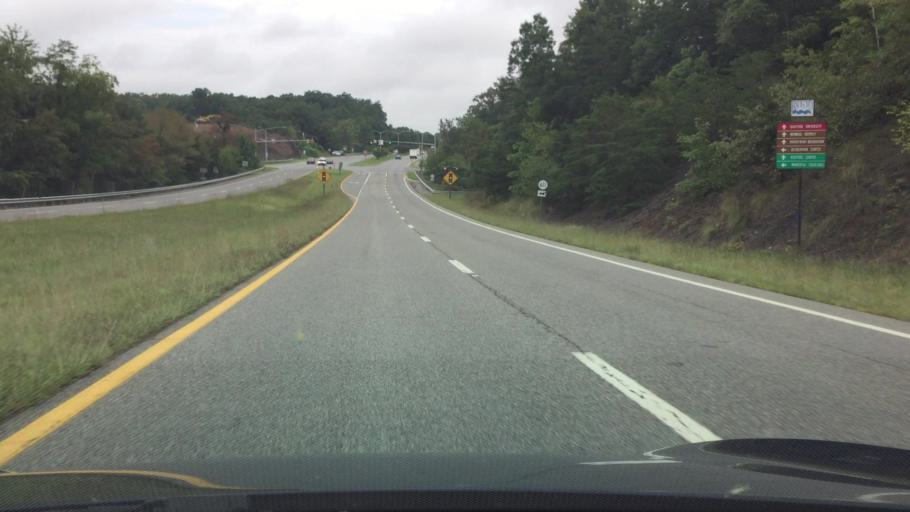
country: US
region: Virginia
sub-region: City of Radford
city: Radford
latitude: 37.1176
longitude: -80.5305
